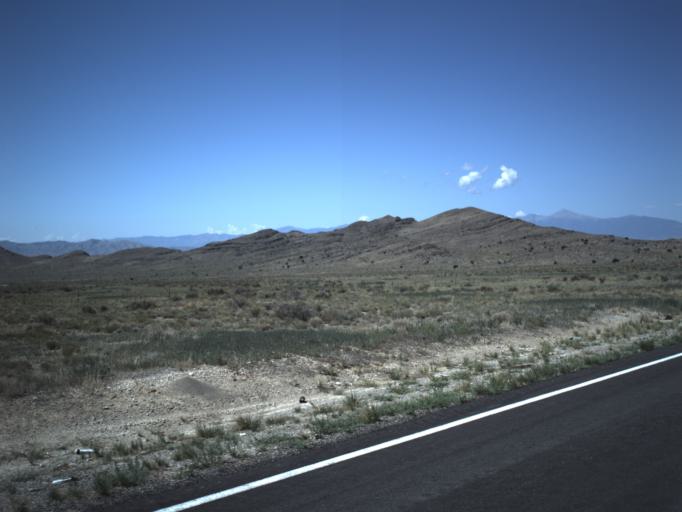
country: US
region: Utah
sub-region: Beaver County
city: Milford
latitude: 39.0760
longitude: -113.6819
